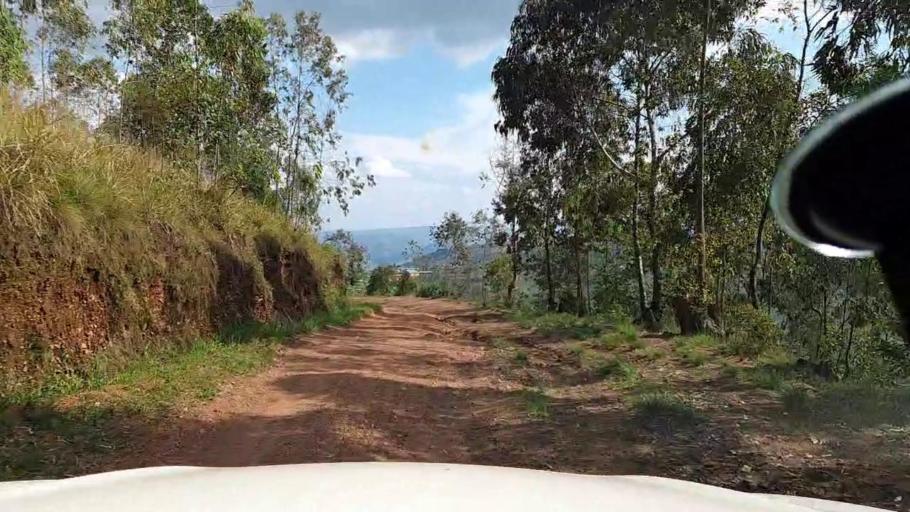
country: RW
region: Kigali
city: Kigali
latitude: -1.7891
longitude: 29.8401
